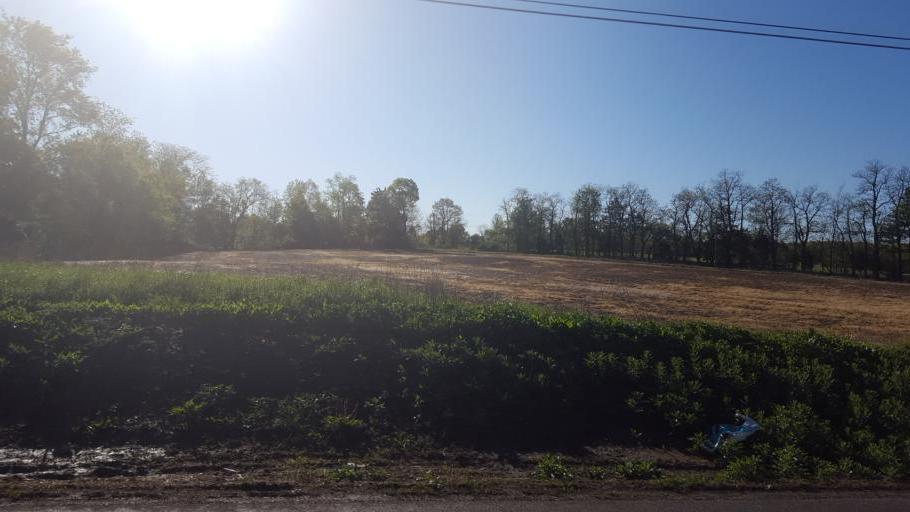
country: US
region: Ohio
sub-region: Delaware County
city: Sunbury
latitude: 40.3118
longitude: -82.8462
